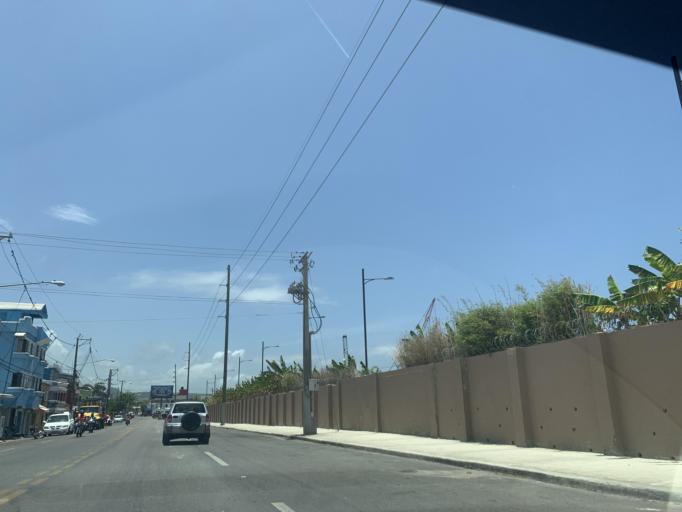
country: DO
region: Puerto Plata
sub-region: Puerto Plata
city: Puerto Plata
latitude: 19.7974
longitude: -70.6997
